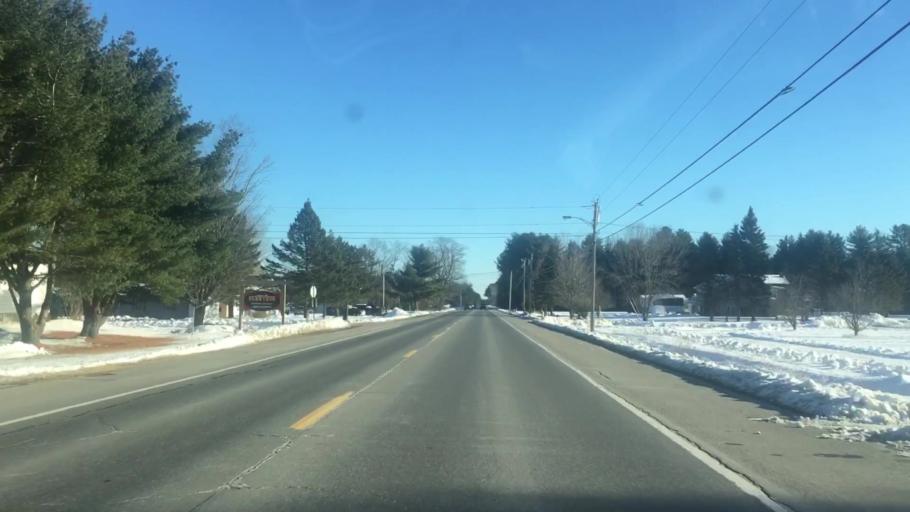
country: US
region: Maine
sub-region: Somerset County
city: Norridgewock
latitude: 44.7052
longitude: -69.7702
